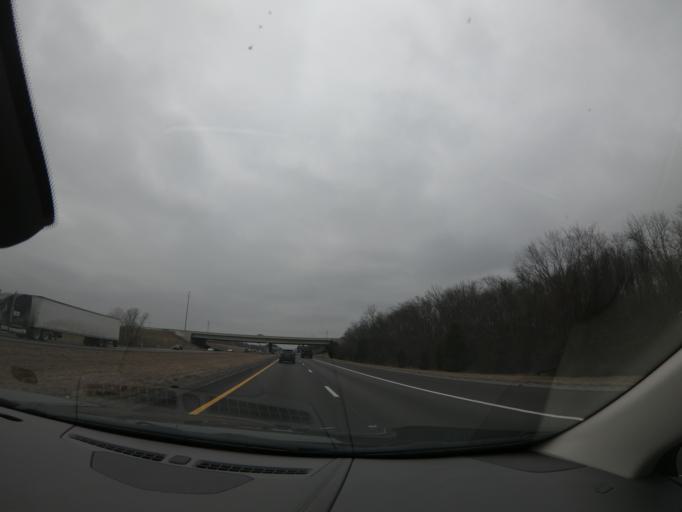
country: US
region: Tennessee
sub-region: Rutherford County
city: Murfreesboro
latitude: 35.7840
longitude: -86.3715
